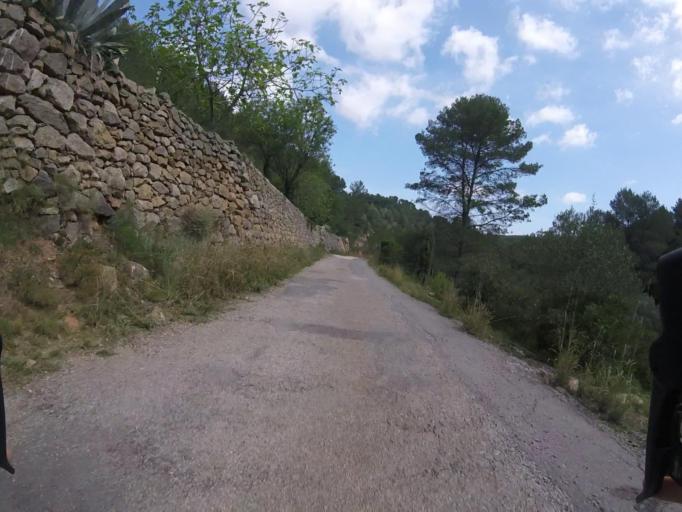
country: ES
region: Valencia
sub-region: Provincia de Castello
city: Cabanes
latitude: 40.1102
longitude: 0.0431
